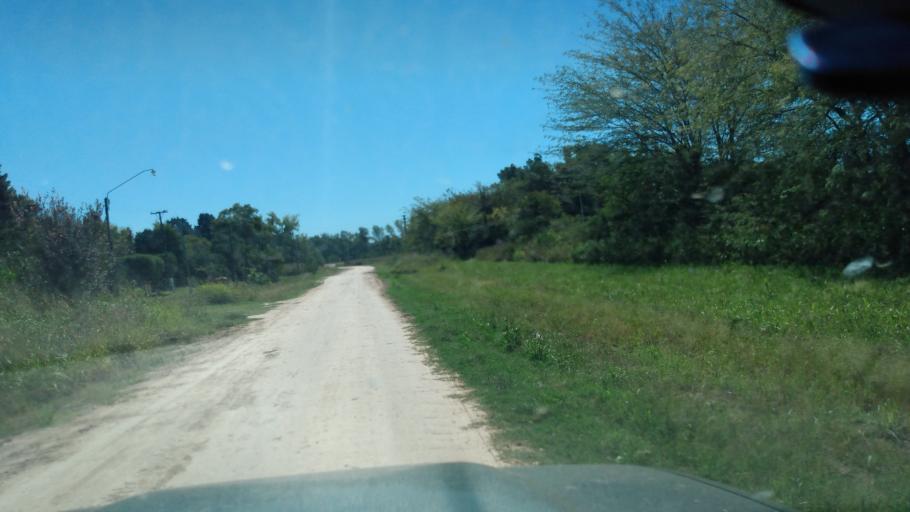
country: AR
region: Buenos Aires
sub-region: Partido de Lujan
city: Lujan
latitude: -34.5506
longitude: -59.1467
